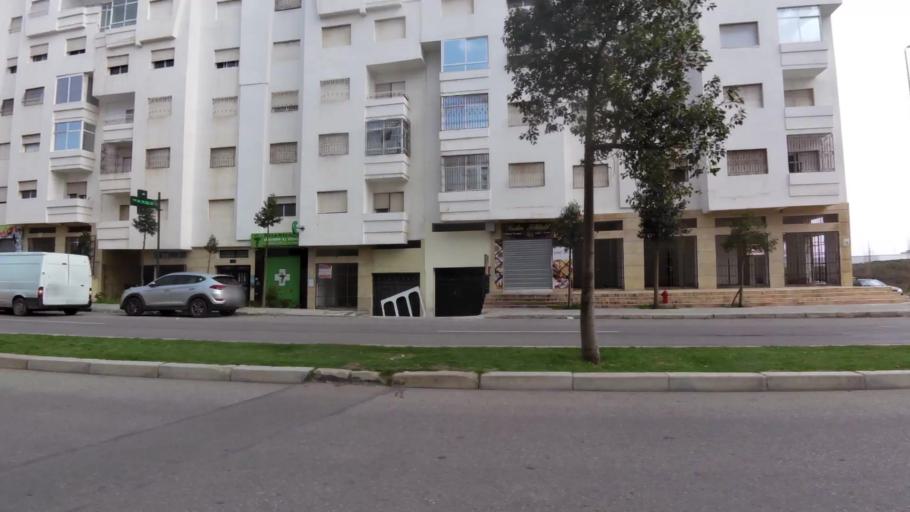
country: MA
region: Tanger-Tetouan
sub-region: Tanger-Assilah
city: Boukhalef
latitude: 35.7460
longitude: -5.8512
